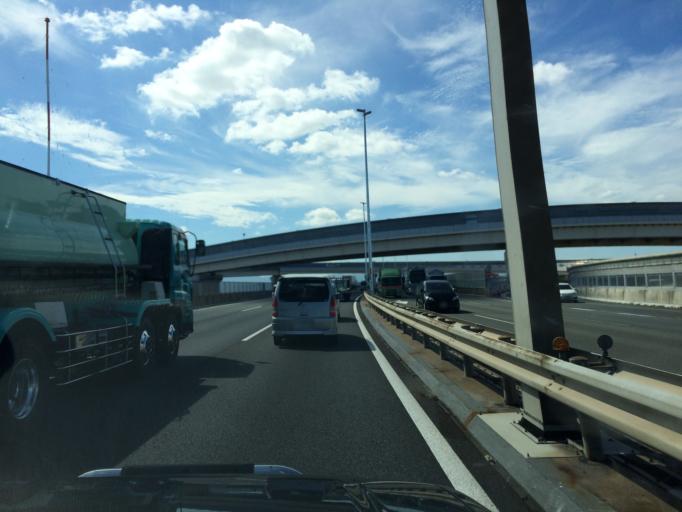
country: JP
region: Osaka
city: Matsubara
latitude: 34.5543
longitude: 135.5661
